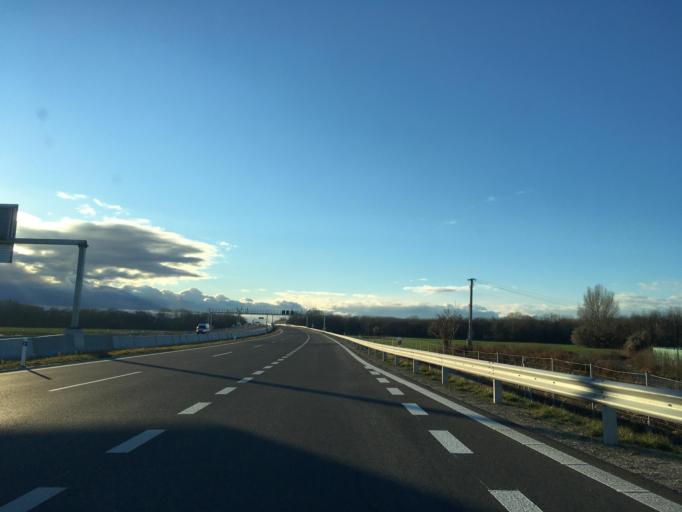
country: SK
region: Bratislavsky
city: Dunajska Luzna
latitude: 48.0893
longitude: 17.1762
